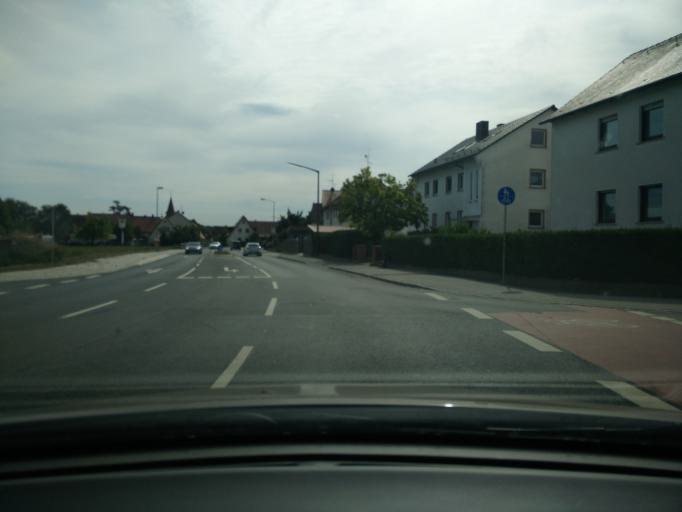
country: DE
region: Bavaria
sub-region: Regierungsbezirk Mittelfranken
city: Seukendorf
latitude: 49.4901
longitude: 10.8768
